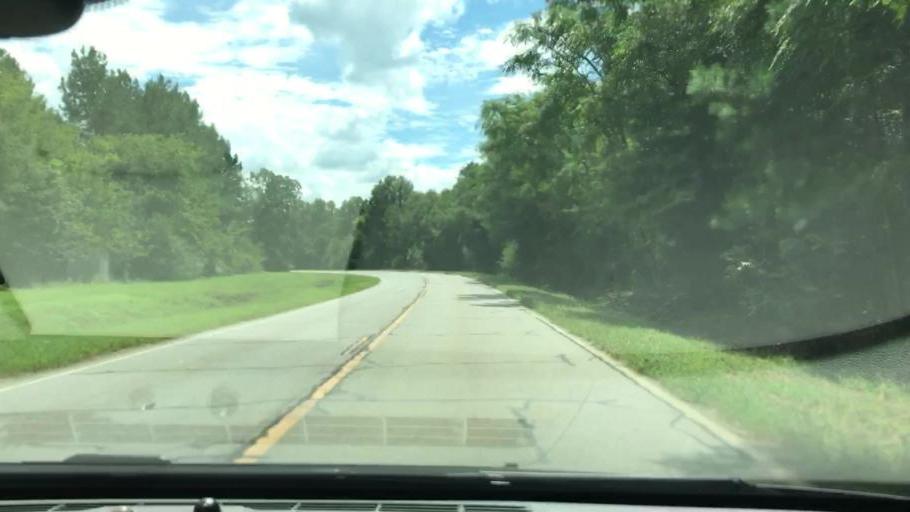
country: US
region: Georgia
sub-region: Quitman County
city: Georgetown
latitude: 32.0472
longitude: -85.0368
